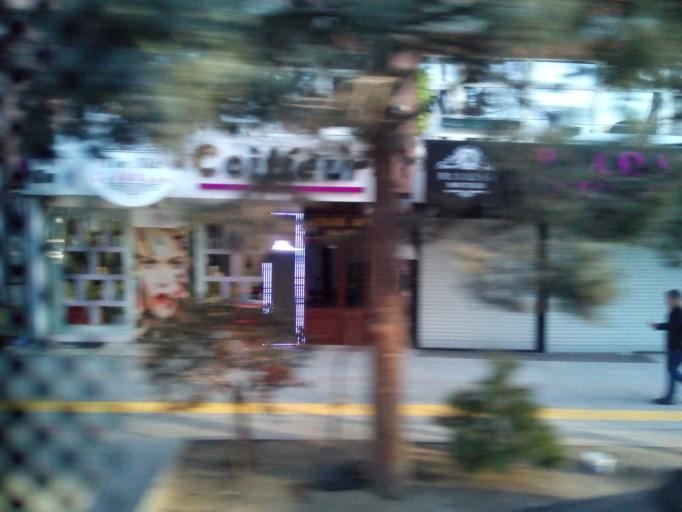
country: TR
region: Ankara
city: Ankara
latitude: 39.9320
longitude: 32.8436
